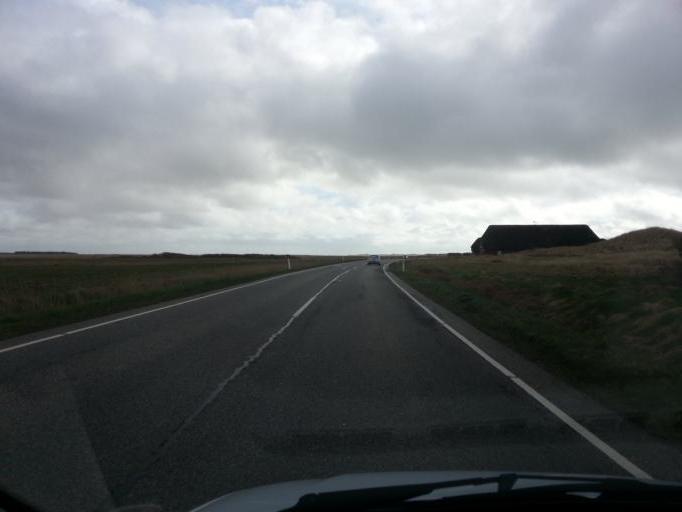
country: DK
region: Central Jutland
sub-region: Ringkobing-Skjern Kommune
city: Ringkobing
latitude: 56.2185
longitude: 8.1390
